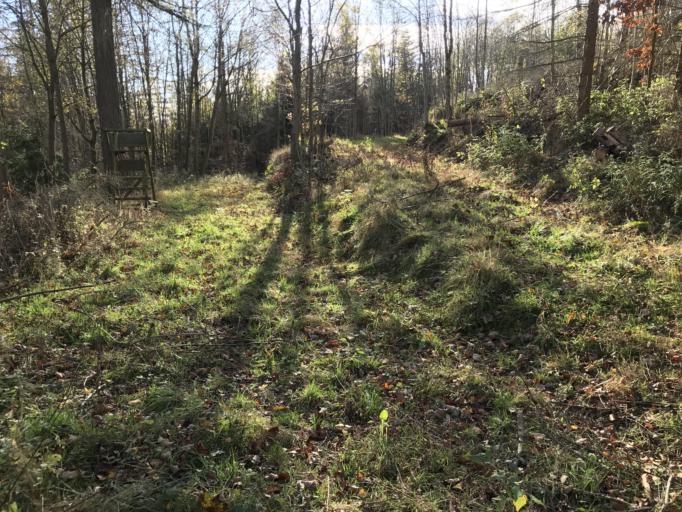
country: DE
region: Saxony-Anhalt
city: Huttenrode
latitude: 51.7567
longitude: 10.8933
